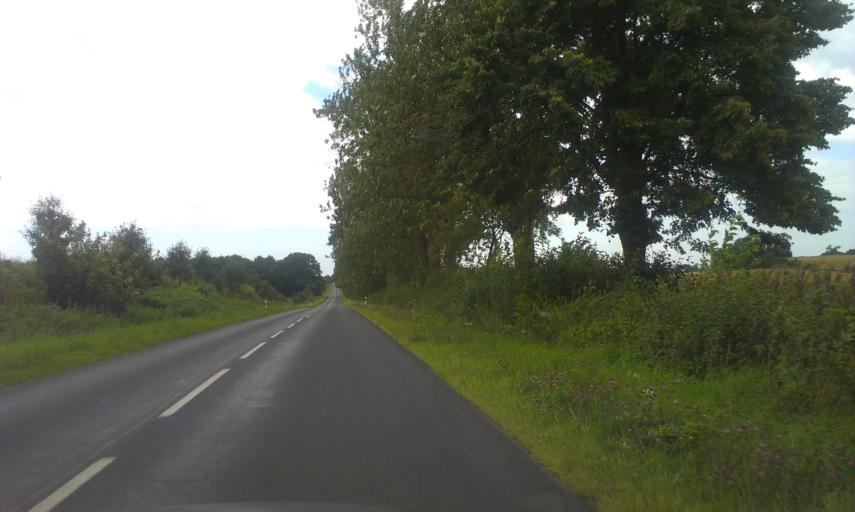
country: PL
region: West Pomeranian Voivodeship
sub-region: Powiat bialogardzki
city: Karlino
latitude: 54.1028
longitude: 15.8297
